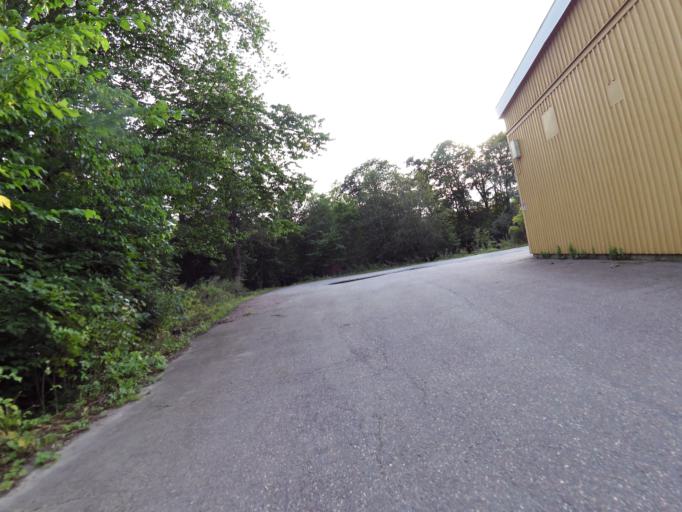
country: SE
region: Gaevleborg
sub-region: Gavle Kommun
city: Gavle
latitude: 60.6971
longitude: 17.1590
